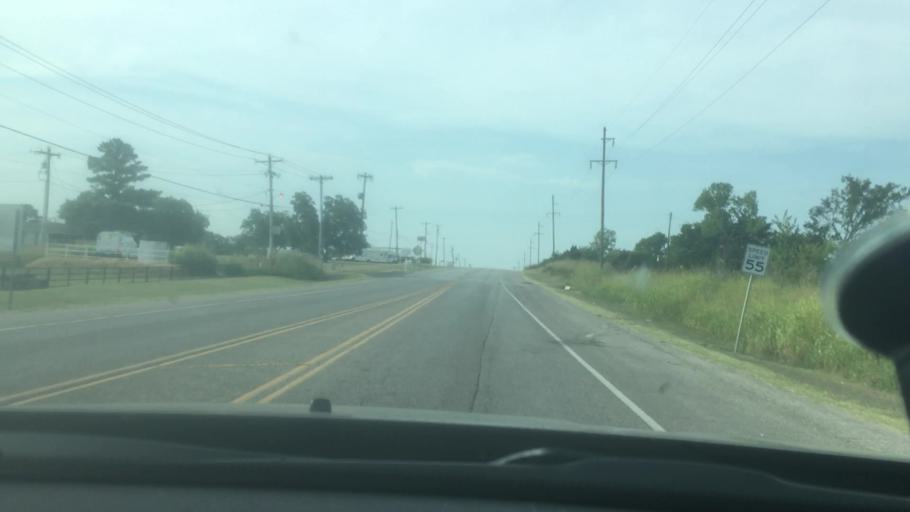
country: US
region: Oklahoma
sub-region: Carter County
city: Ardmore
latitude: 34.1374
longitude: -97.1431
